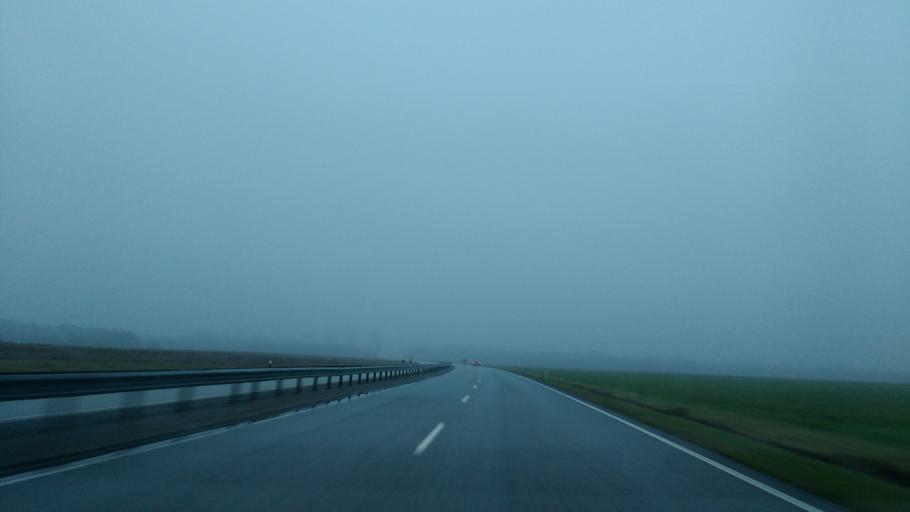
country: DE
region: Schleswig-Holstein
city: Jevenstedt
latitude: 54.2474
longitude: 9.6691
